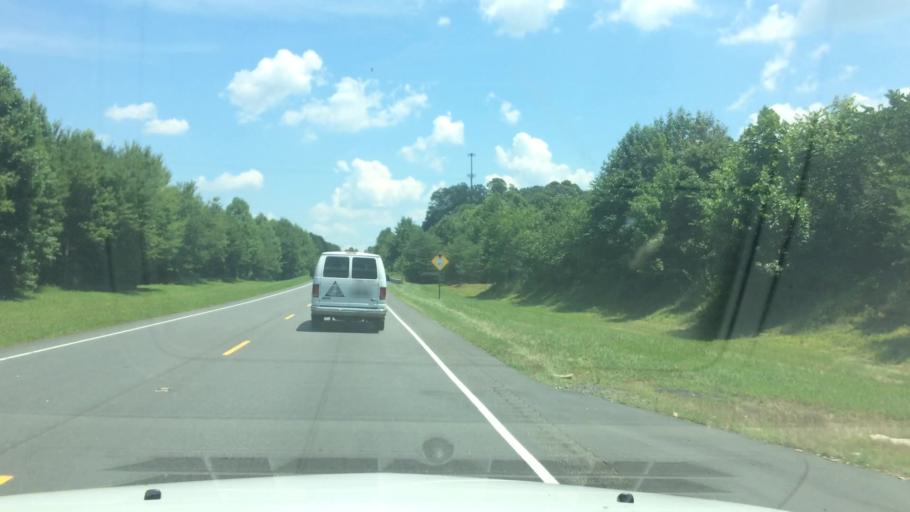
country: US
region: North Carolina
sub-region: Iredell County
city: Statesville
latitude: 35.8028
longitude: -80.9520
